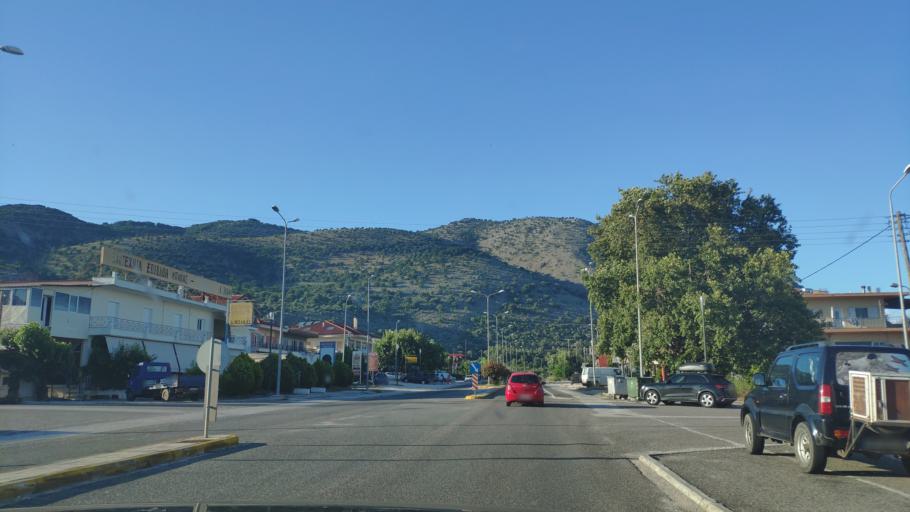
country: GR
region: Epirus
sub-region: Nomos Prevezis
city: Louros
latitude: 39.1688
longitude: 20.7596
